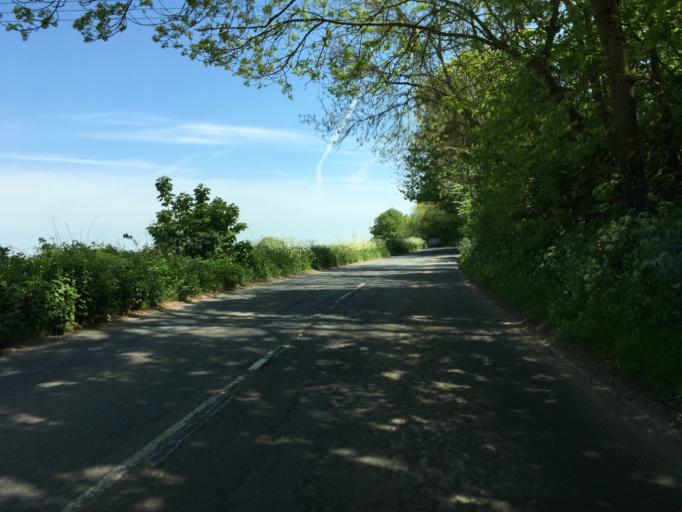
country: GB
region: England
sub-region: Gloucestershire
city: Nailsworth
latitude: 51.6836
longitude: -2.2491
